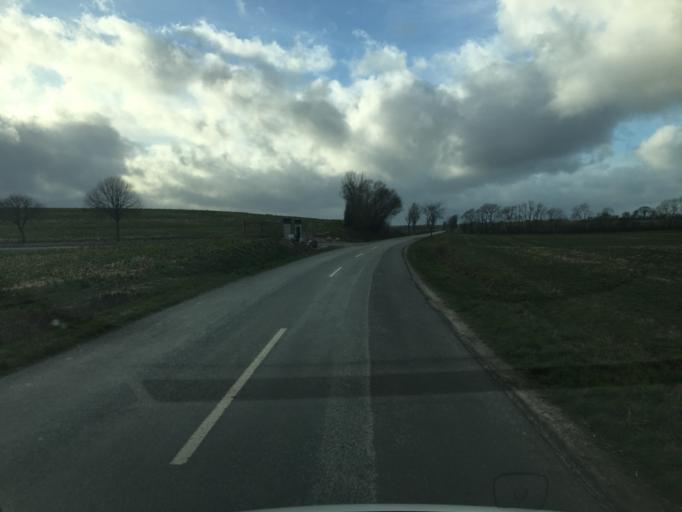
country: DK
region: South Denmark
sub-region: Sonderborg Kommune
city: Grasten
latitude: 54.9627
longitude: 9.5440
